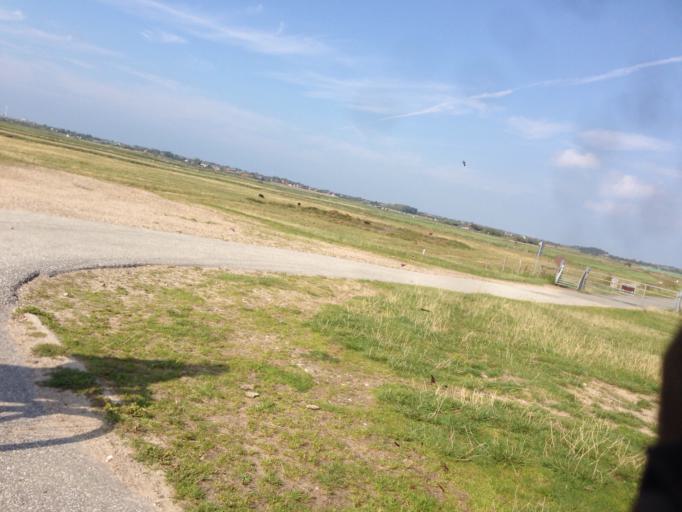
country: DE
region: Schleswig-Holstein
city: Tinnum
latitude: 54.8819
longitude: 8.3411
